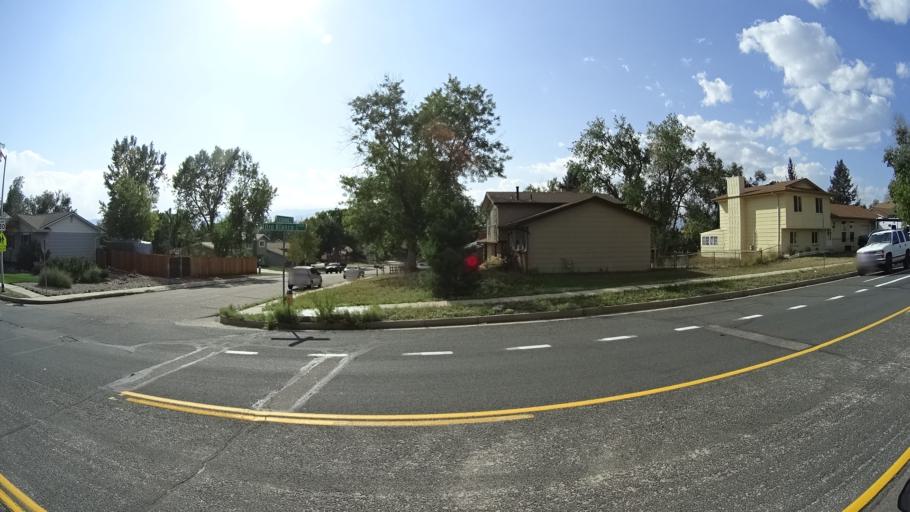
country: US
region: Colorado
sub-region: El Paso County
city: Cimarron Hills
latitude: 38.8779
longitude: -104.7400
